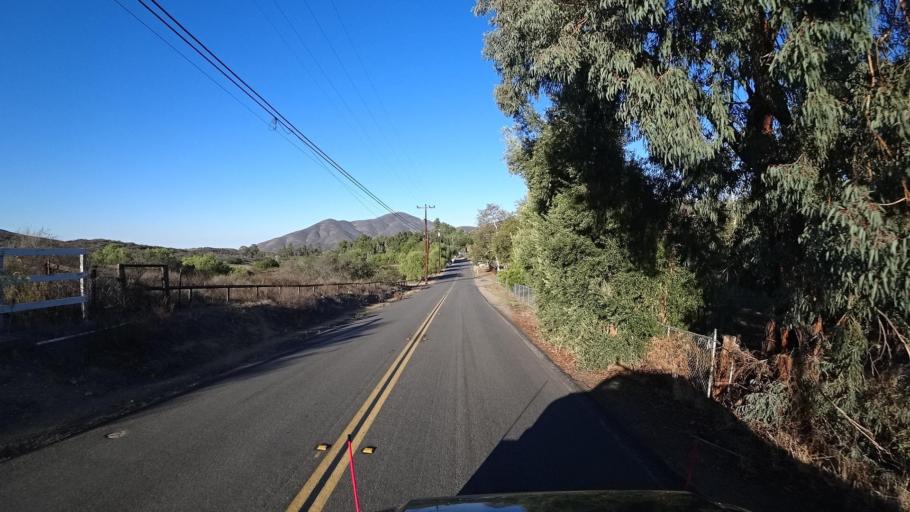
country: US
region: California
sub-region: San Diego County
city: Jamul
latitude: 32.7065
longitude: -116.8850
